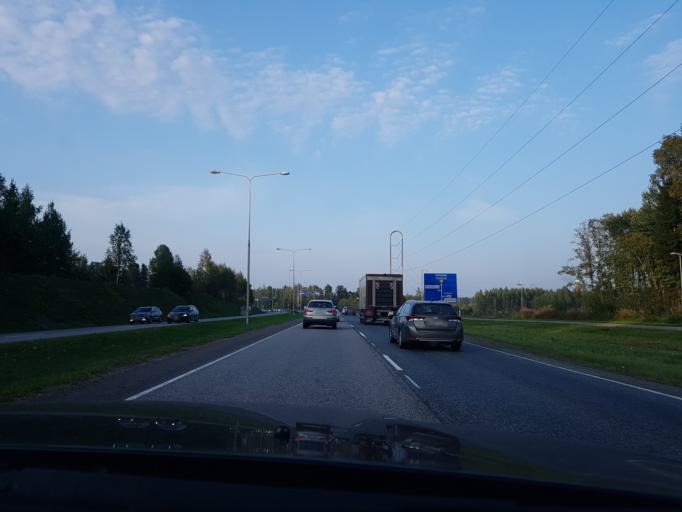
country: FI
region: Uusimaa
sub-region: Helsinki
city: Tuusula
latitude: 60.3708
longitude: 25.0150
